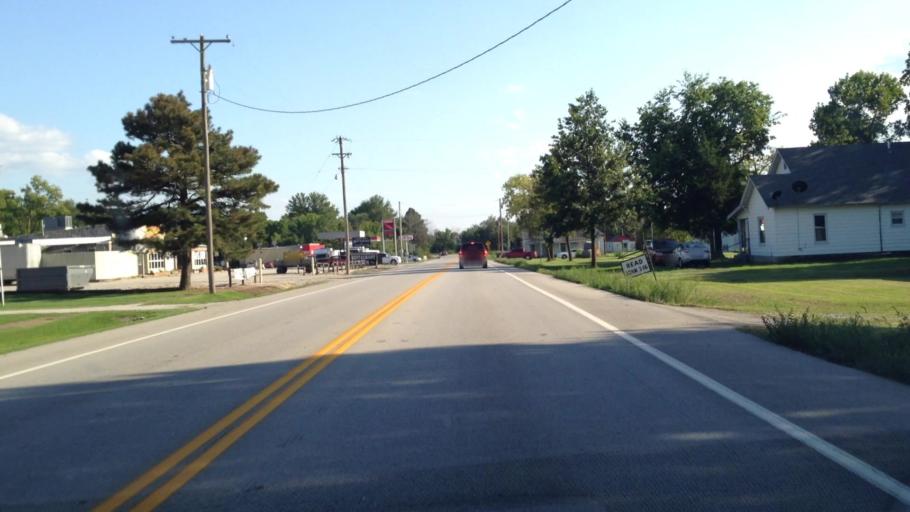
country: US
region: Missouri
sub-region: Jasper County
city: Carl Junction
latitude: 37.2757
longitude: -94.6011
